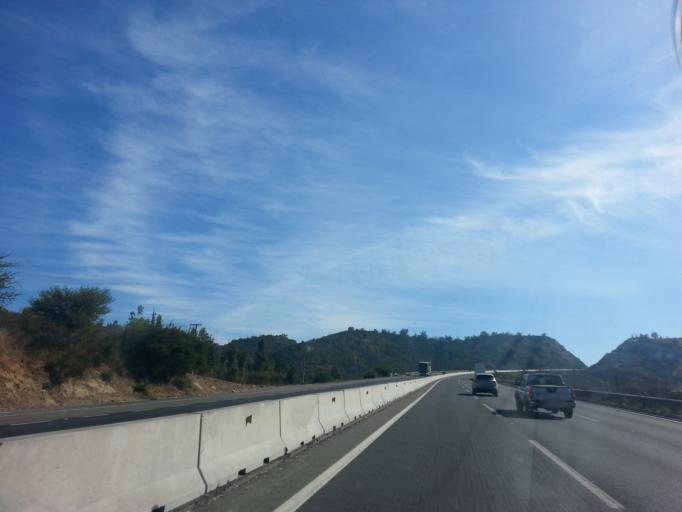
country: CL
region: Valparaiso
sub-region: Provincia de Marga Marga
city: Quilpue
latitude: -33.2945
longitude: -71.4208
